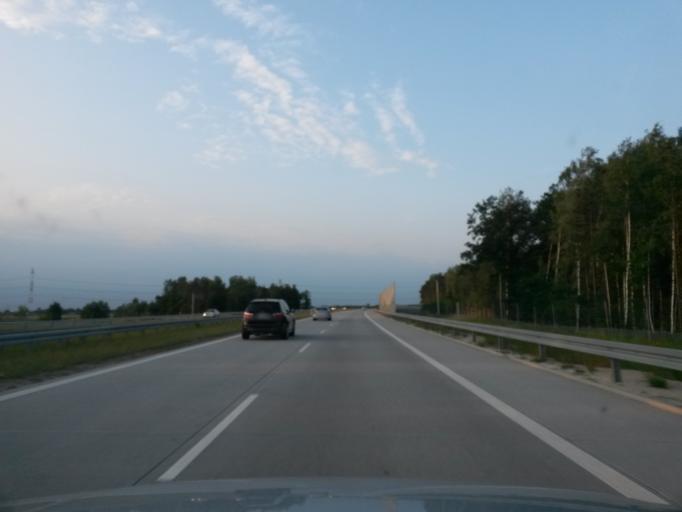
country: PL
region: Lodz Voivodeship
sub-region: Powiat sieradzki
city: Zloczew
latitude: 51.3796
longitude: 18.5500
